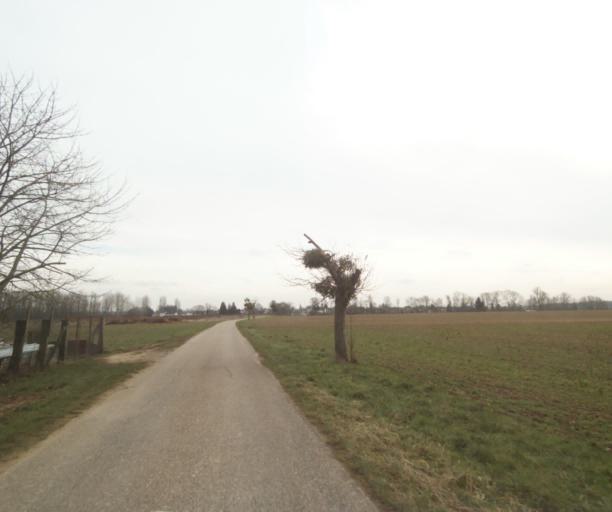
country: FR
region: Champagne-Ardenne
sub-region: Departement de la Haute-Marne
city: Villiers-en-Lieu
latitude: 48.6711
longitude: 4.8873
